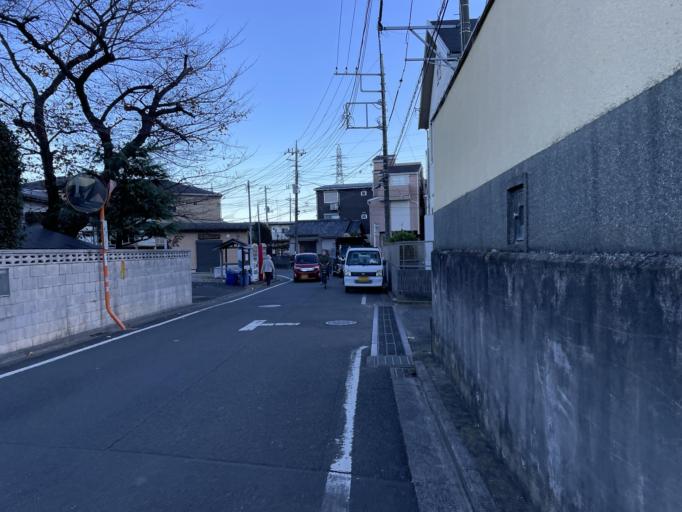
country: JP
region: Saitama
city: Wako
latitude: 35.7944
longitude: 139.6245
